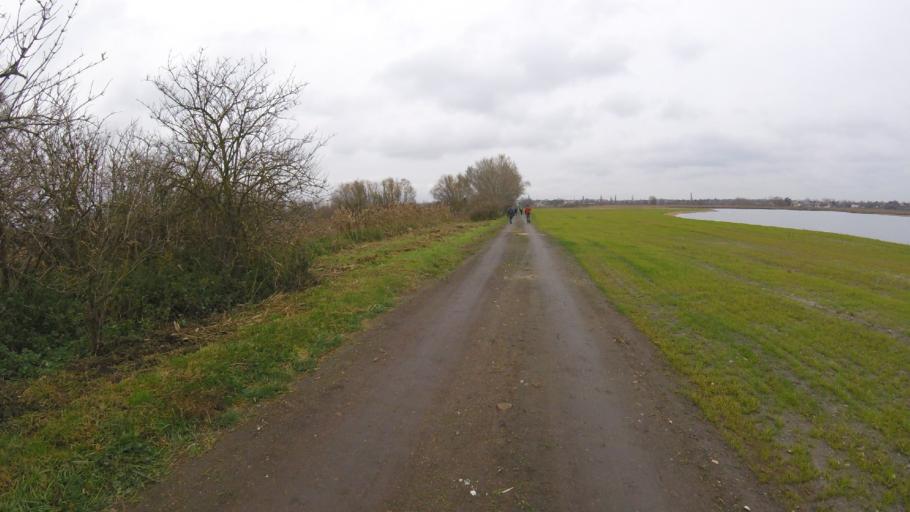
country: HU
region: Komarom-Esztergom
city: Tata
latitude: 47.6580
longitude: 18.3047
